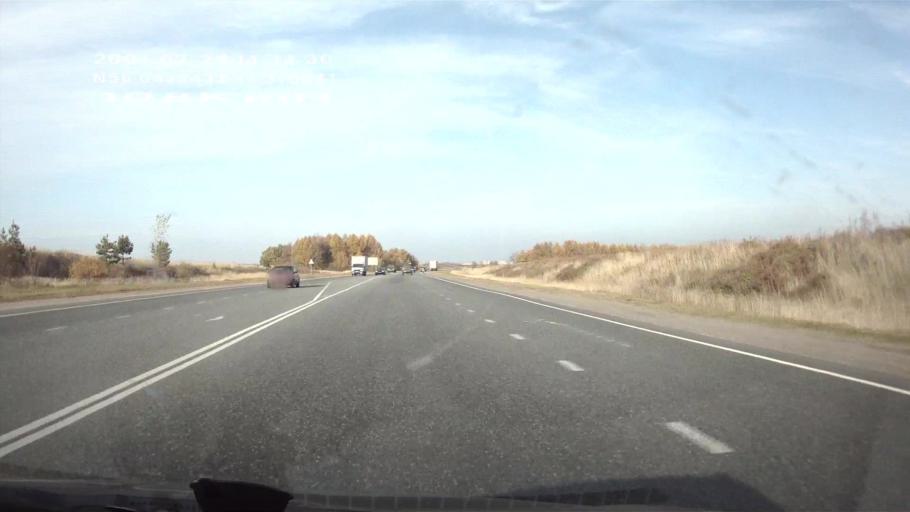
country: RU
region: Chuvashia
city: Kugesi
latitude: 56.0470
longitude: 47.3704
